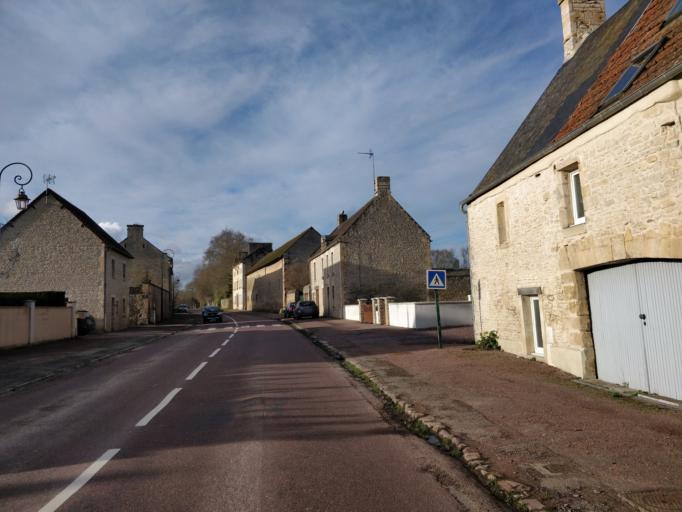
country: FR
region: Lower Normandy
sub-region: Departement du Calvados
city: Rots
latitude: 49.2007
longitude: -0.4806
